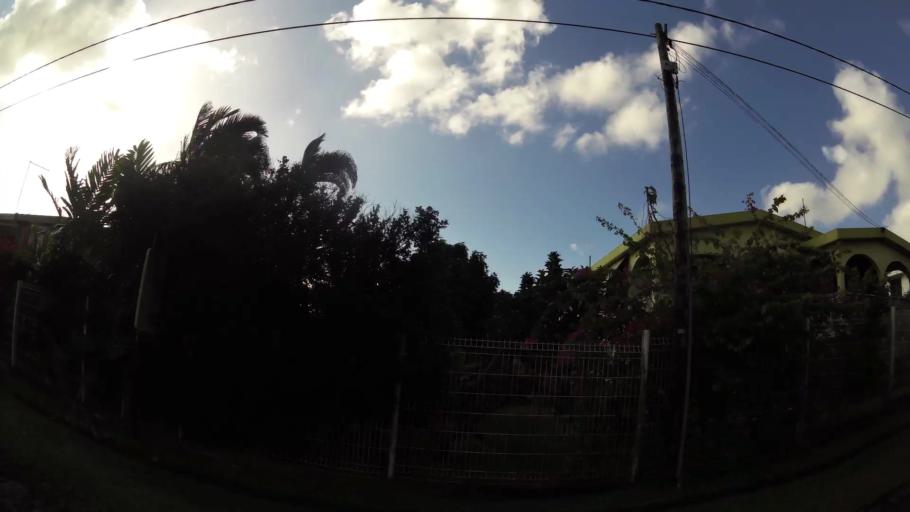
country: MQ
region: Martinique
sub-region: Martinique
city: Le Lamentin
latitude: 14.6244
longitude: -61.0142
